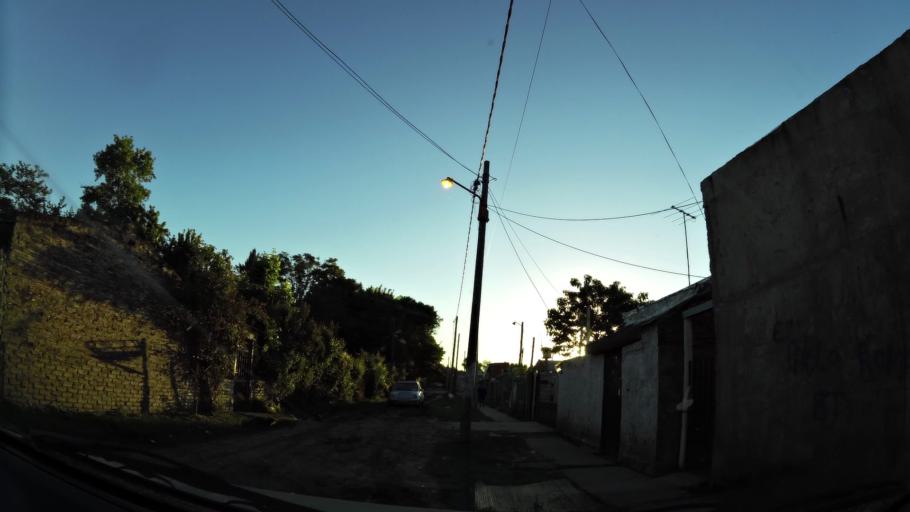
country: AR
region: Buenos Aires
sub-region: Partido de Almirante Brown
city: Adrogue
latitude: -34.7869
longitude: -58.3386
